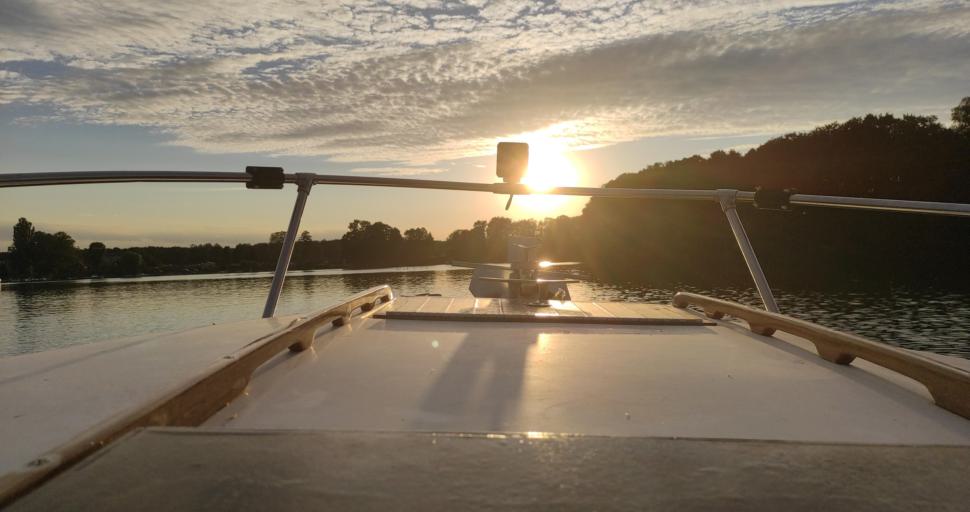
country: DE
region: Brandenburg
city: Friedland
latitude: 52.0227
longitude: 14.1839
